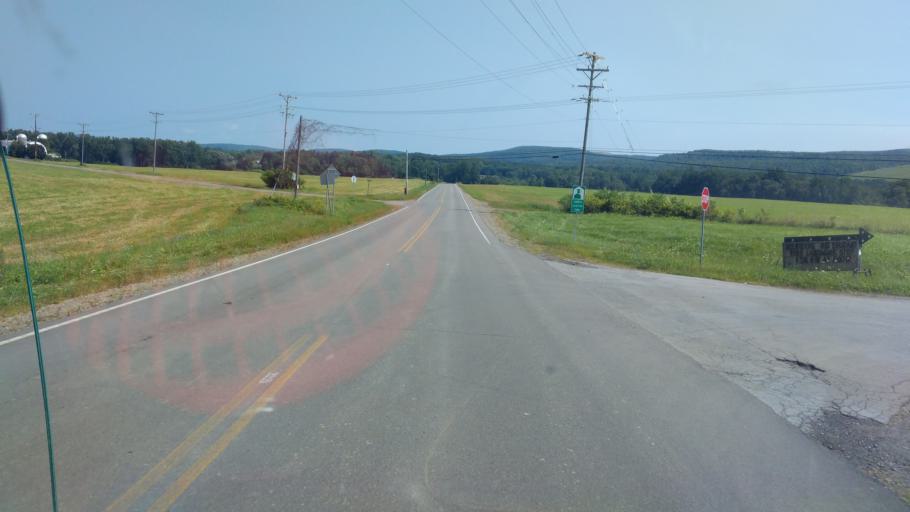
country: US
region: New York
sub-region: Allegany County
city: Belmont
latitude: 42.2555
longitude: -78.0584
